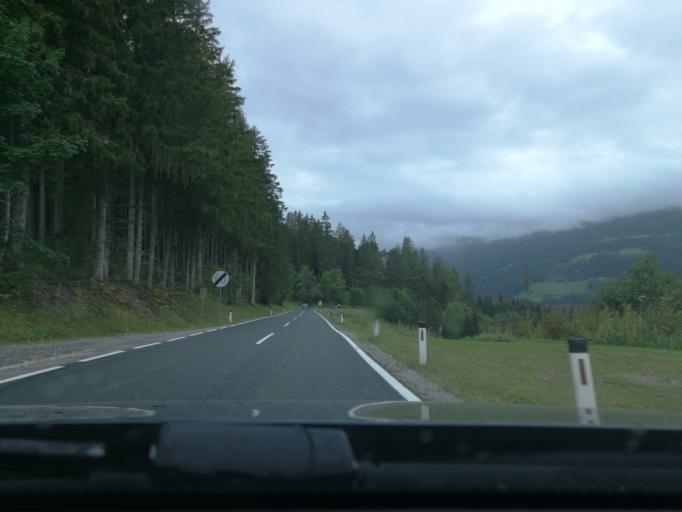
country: AT
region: Salzburg
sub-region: Politischer Bezirk Sankt Johann im Pongau
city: Forstau
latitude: 47.3814
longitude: 13.5054
